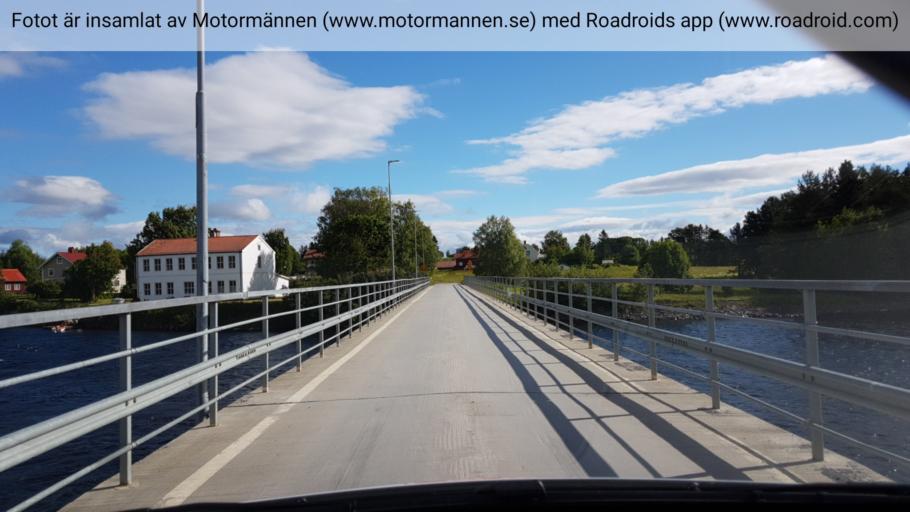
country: SE
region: Jaemtland
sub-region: Krokoms Kommun
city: Krokom
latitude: 63.2985
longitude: 14.4599
